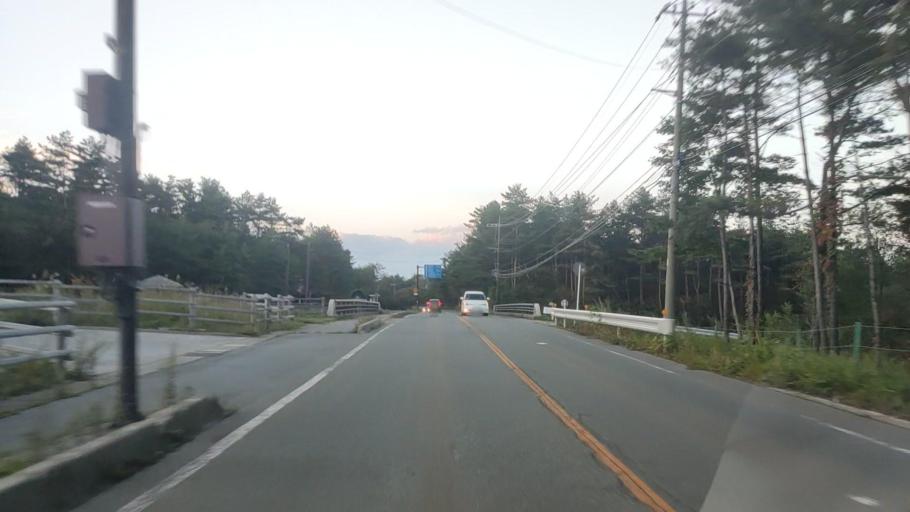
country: JP
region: Nagano
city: Komoro
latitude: 36.4287
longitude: 138.5712
